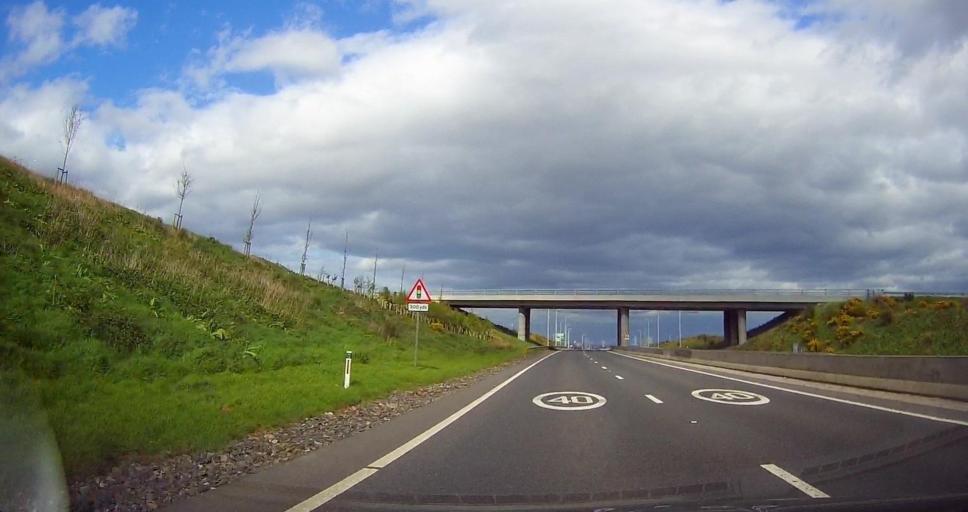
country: GB
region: Scotland
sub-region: Aberdeenshire
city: Portlethen
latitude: 57.0930
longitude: -2.1203
